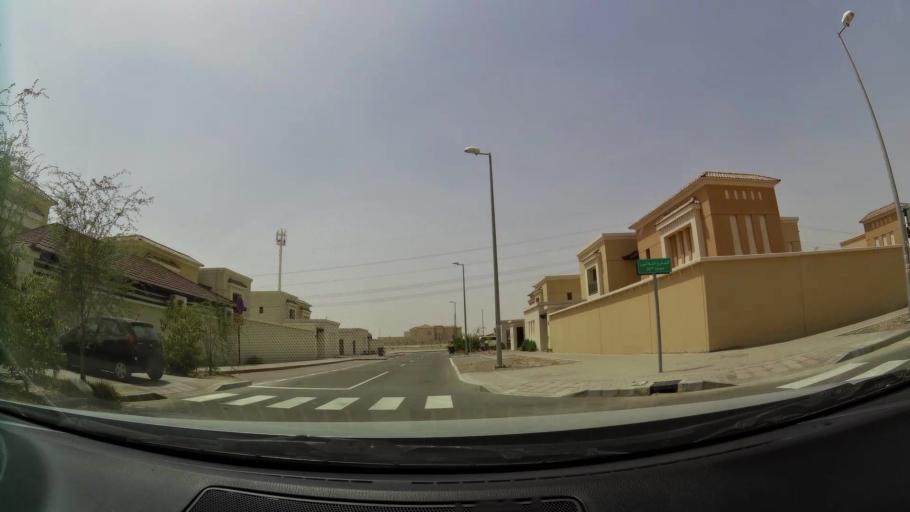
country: AE
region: Abu Dhabi
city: Al Ain
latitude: 24.1516
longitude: 55.6348
